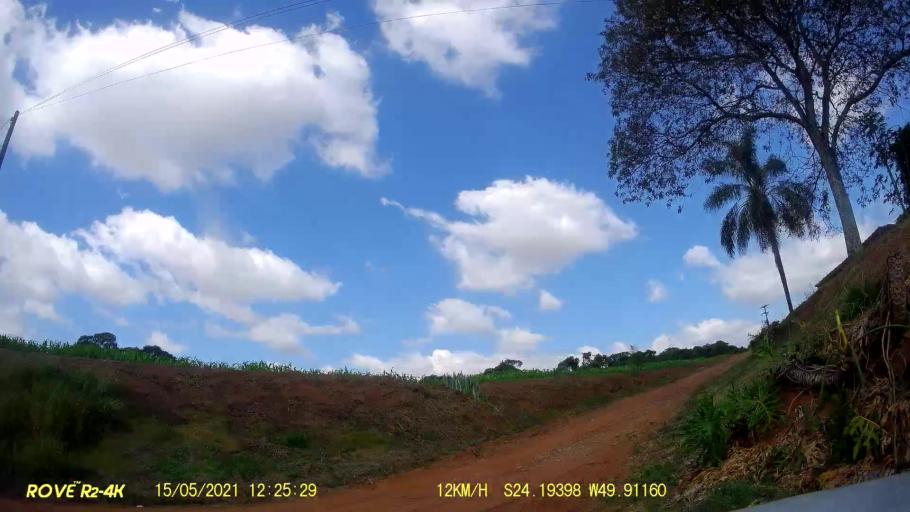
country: BR
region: Parana
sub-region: Jaguariaiva
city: Jaguariaiva
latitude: -24.1939
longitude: -49.9116
